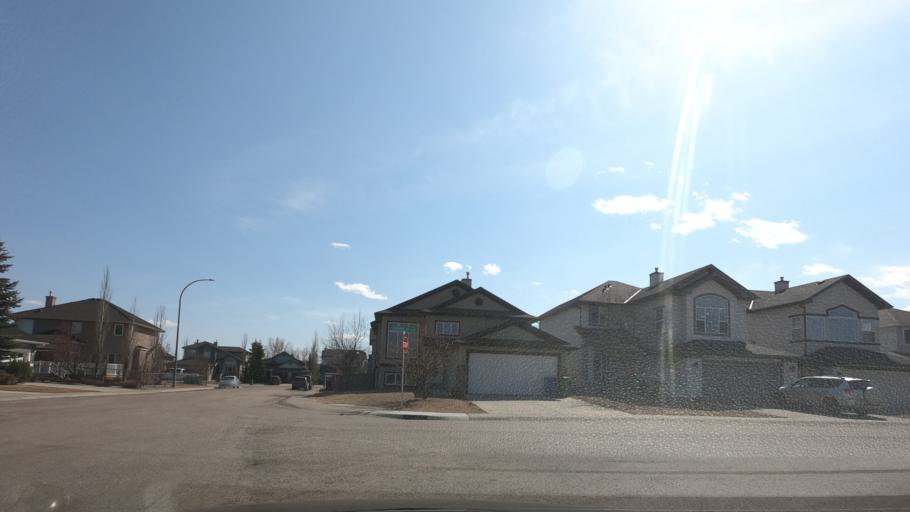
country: CA
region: Alberta
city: Airdrie
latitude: 51.2970
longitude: -114.0463
